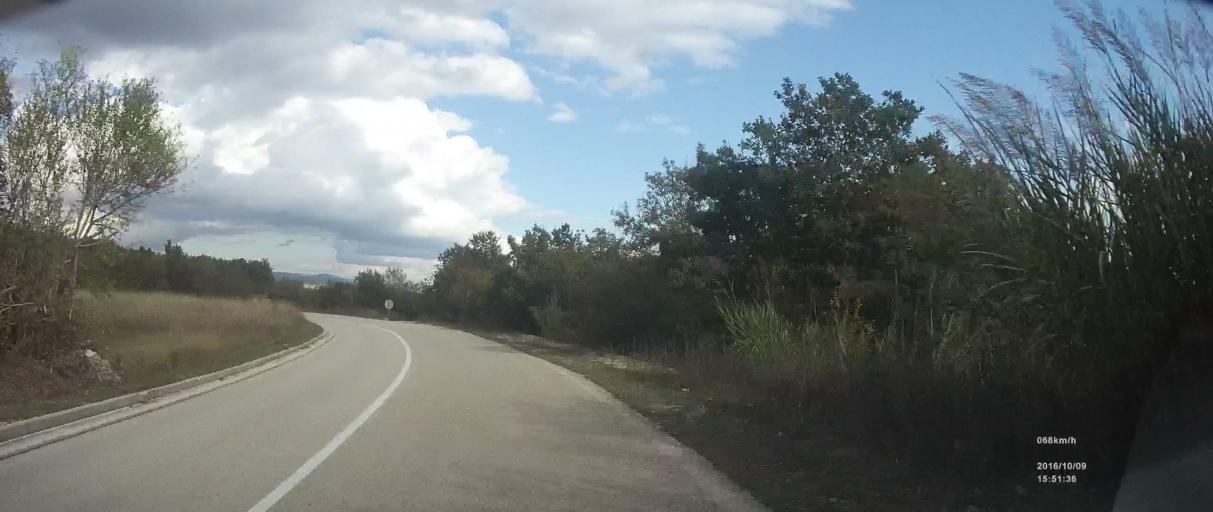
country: HR
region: Splitsko-Dalmatinska
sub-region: Grad Trogir
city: Trogir
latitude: 43.6054
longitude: 16.2132
